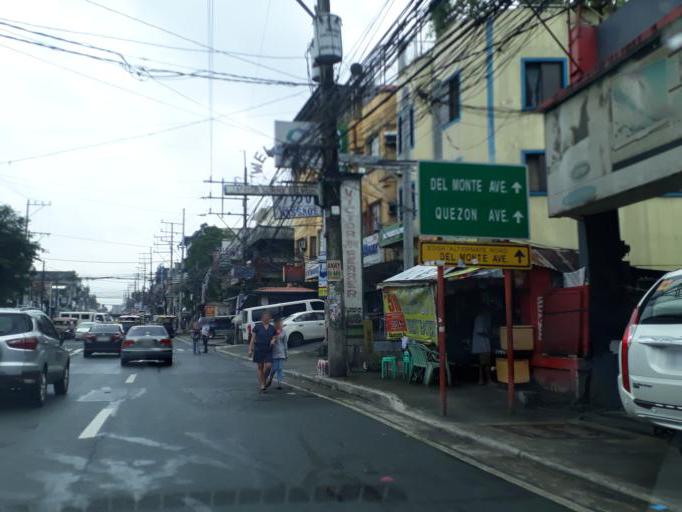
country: PH
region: Calabarzon
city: Del Monte
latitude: 14.6550
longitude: 121.0186
